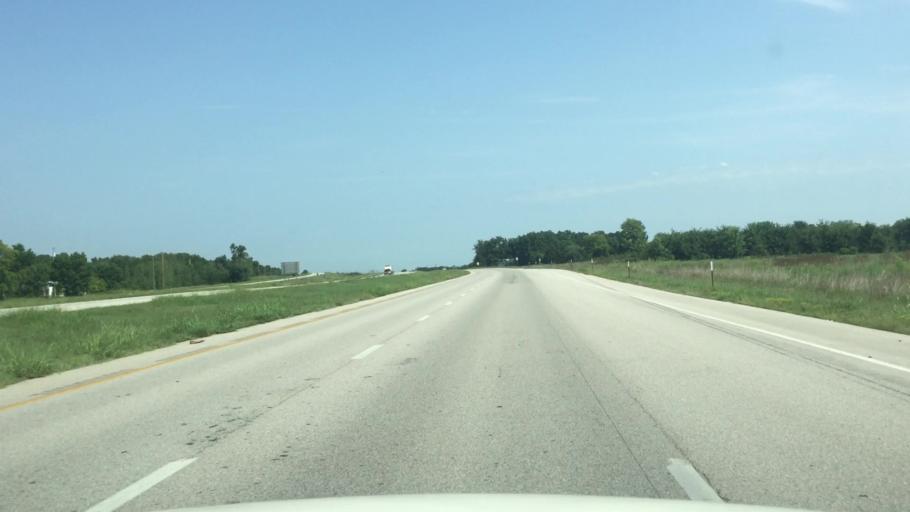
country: US
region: Kansas
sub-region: Montgomery County
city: Coffeyville
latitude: 37.0510
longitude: -95.5810
